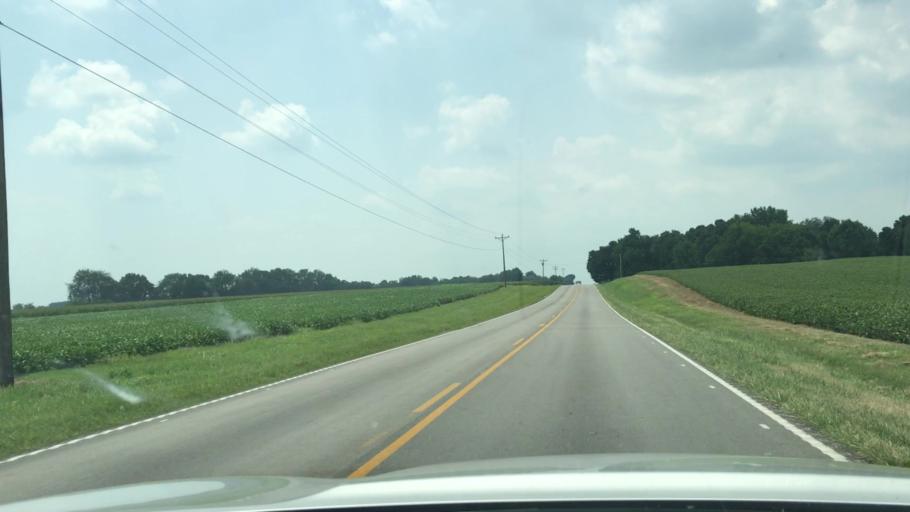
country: US
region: Kentucky
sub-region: Todd County
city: Guthrie
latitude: 36.6929
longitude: -87.1277
